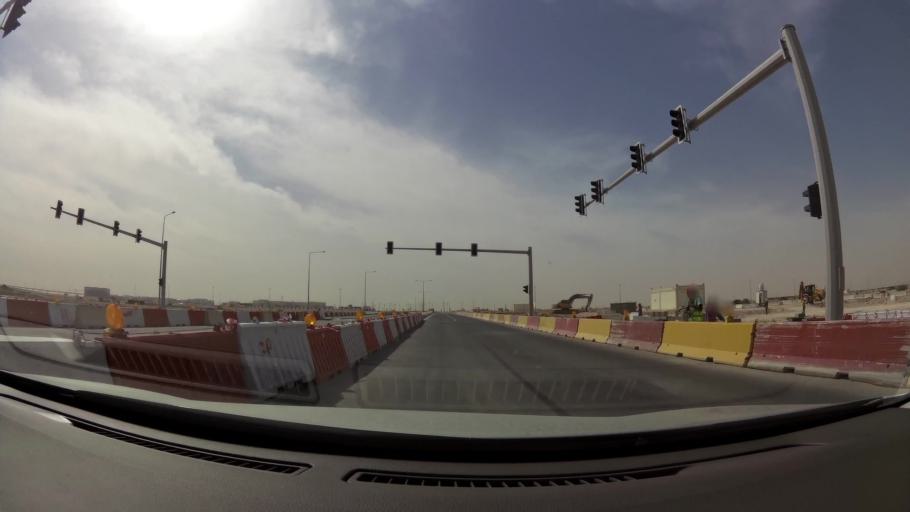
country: QA
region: Baladiyat ar Rayyan
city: Ar Rayyan
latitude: 25.3316
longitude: 51.3660
